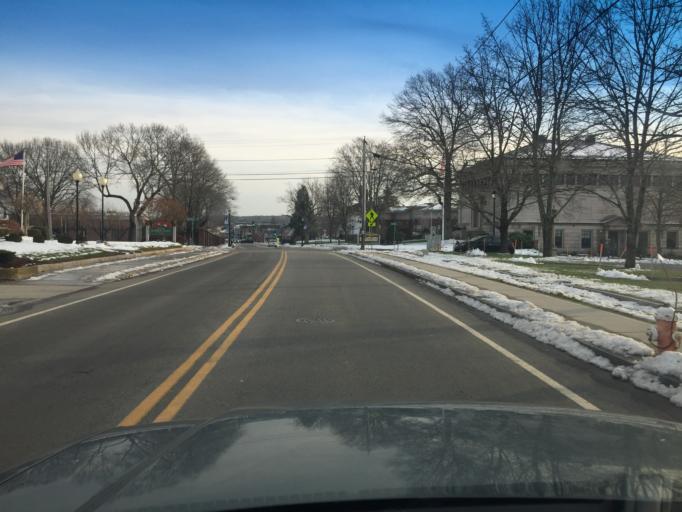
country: US
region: Massachusetts
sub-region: Norfolk County
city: Franklin
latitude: 42.0863
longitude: -71.4000
